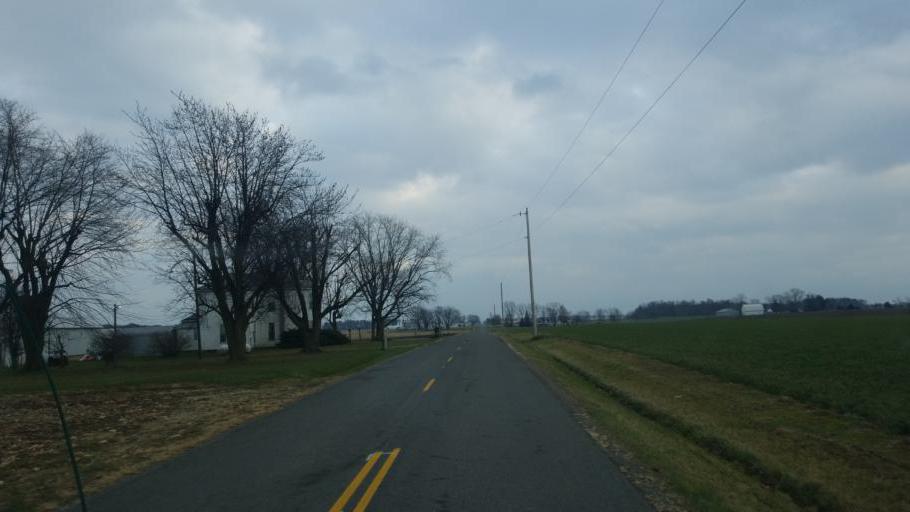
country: US
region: Ohio
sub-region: Mercer County
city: Coldwater
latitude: 40.5090
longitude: -84.6972
